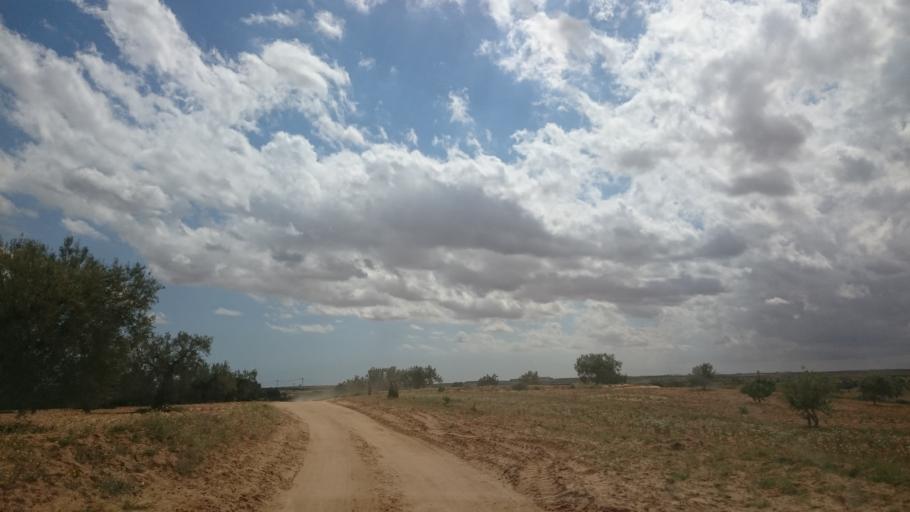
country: TN
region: Safaqis
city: Sfax
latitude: 34.7494
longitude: 10.4867
